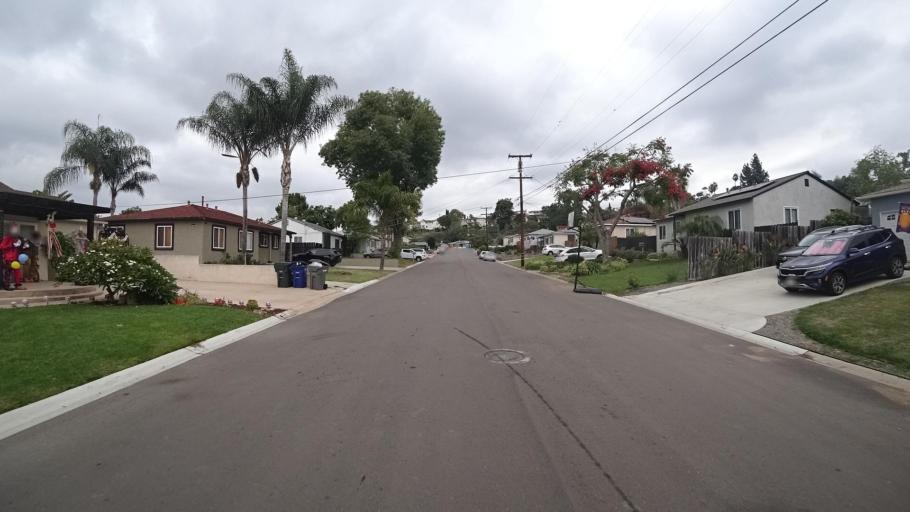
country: US
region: California
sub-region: San Diego County
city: Spring Valley
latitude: 32.7466
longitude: -117.0131
